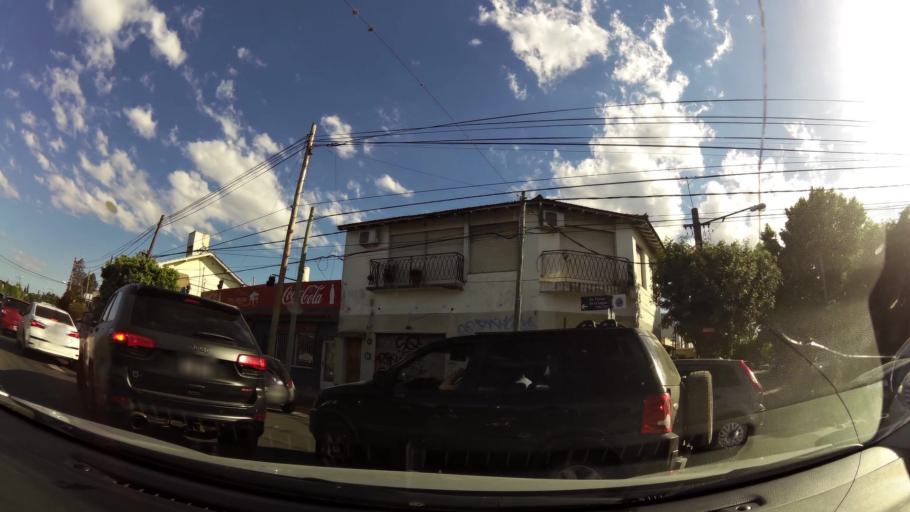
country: AR
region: Buenos Aires
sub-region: Partido de San Isidro
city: San Isidro
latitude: -34.4984
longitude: -58.5437
